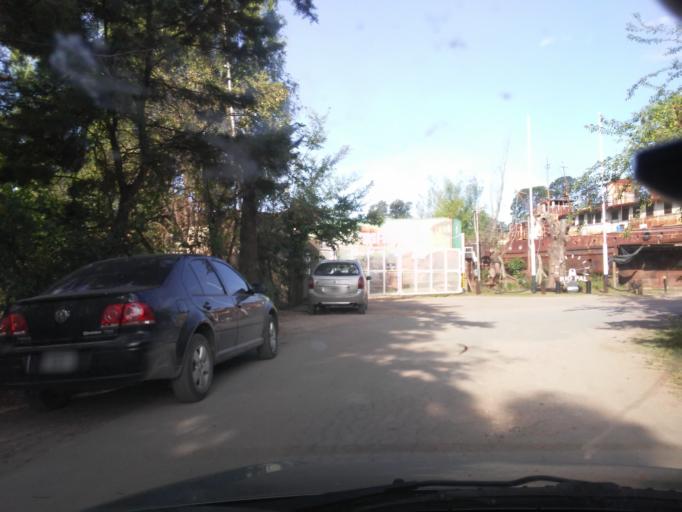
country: AR
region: Buenos Aires
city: Belen de Escobar
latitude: -34.2490
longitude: -58.7266
